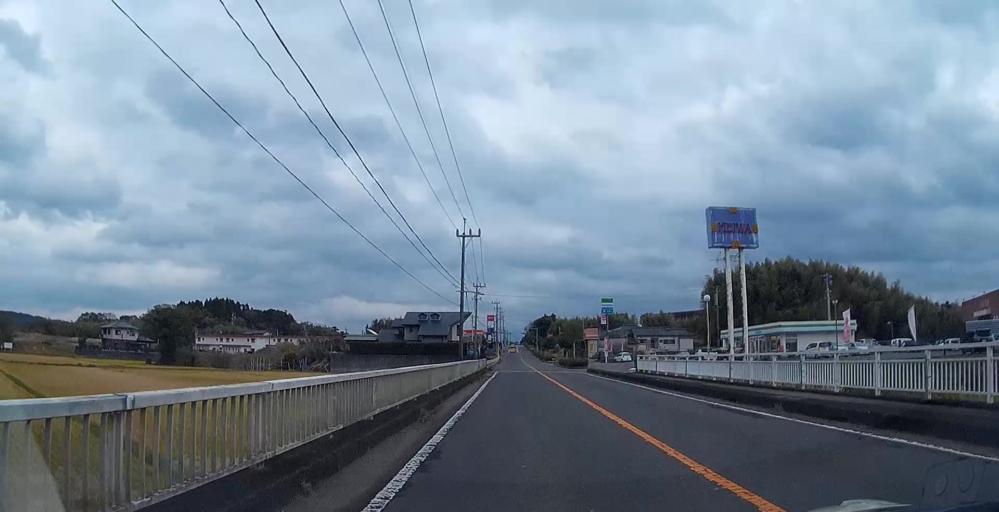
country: JP
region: Kagoshima
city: Akune
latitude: 32.0829
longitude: 130.1998
